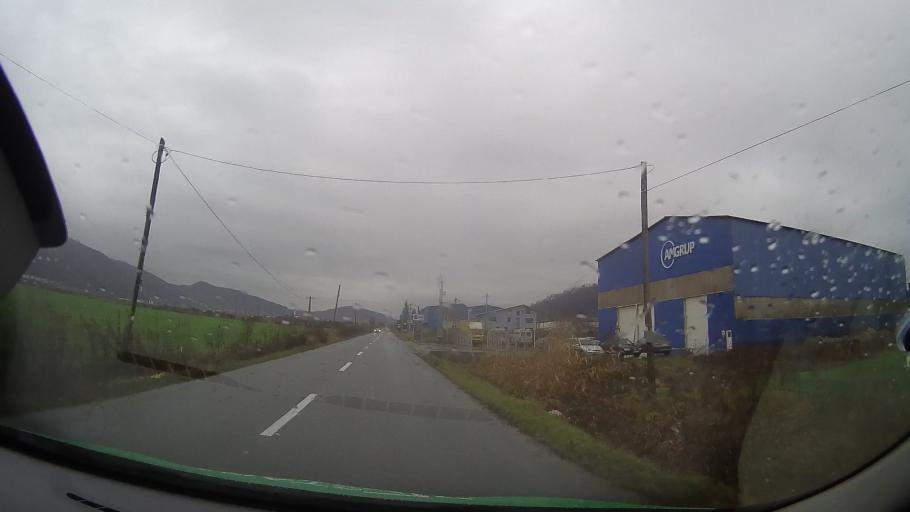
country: RO
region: Bistrita-Nasaud
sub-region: Municipiul Bistrita
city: Viisoara
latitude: 47.0592
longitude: 24.4358
